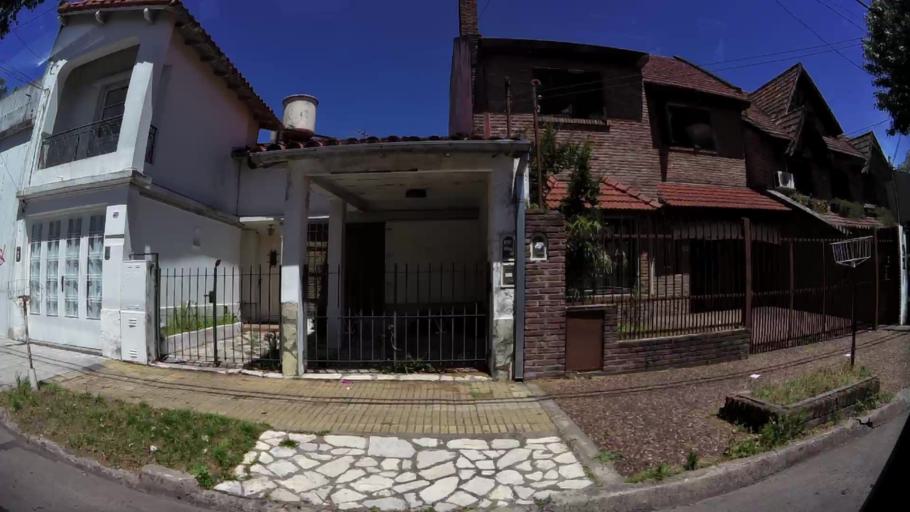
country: AR
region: Buenos Aires
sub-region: Partido de Vicente Lopez
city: Olivos
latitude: -34.5034
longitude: -58.5000
